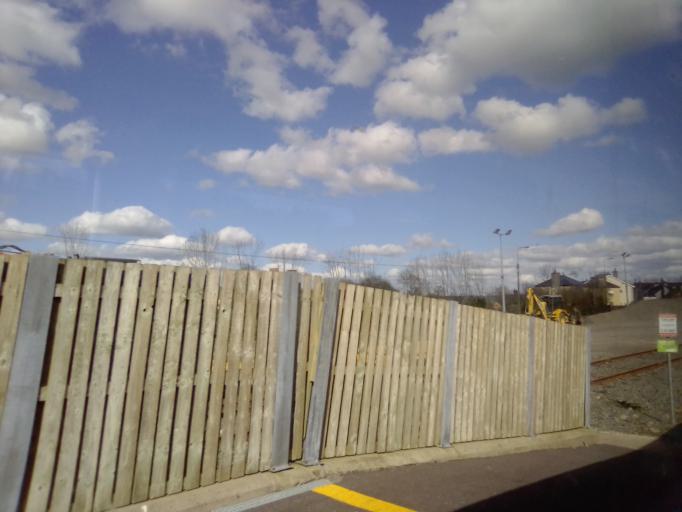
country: IE
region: Munster
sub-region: County Cork
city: Kanturk
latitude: 52.1289
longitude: -8.8980
